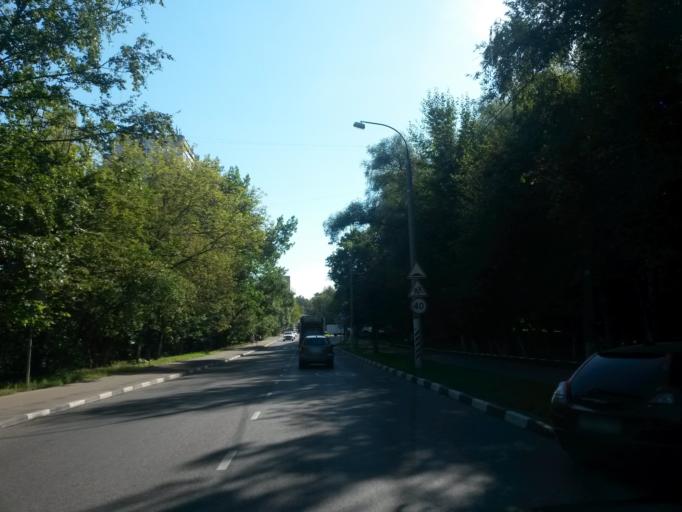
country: RU
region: Moscow
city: Zyuzino
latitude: 55.6572
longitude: 37.5849
